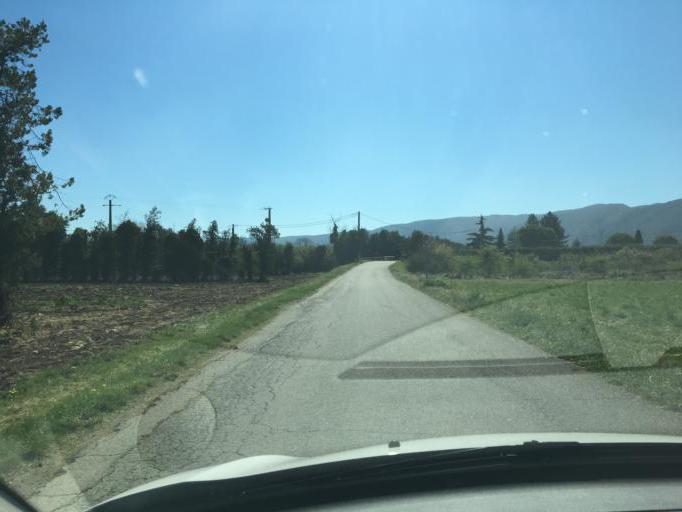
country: FR
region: Provence-Alpes-Cote d'Azur
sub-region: Departement du Vaucluse
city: Robion
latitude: 43.8655
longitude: 5.1225
